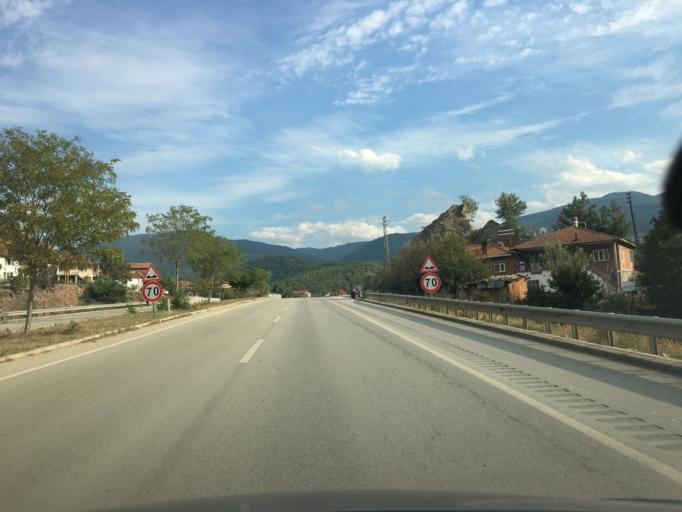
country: TR
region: Karabuk
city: Karabuk
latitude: 41.0973
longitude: 32.6747
